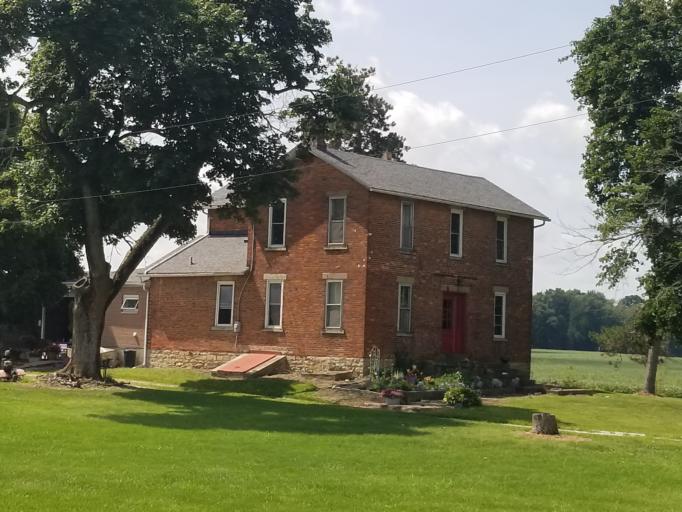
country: US
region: Ohio
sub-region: Delaware County
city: Delaware
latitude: 40.3556
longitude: -83.1257
